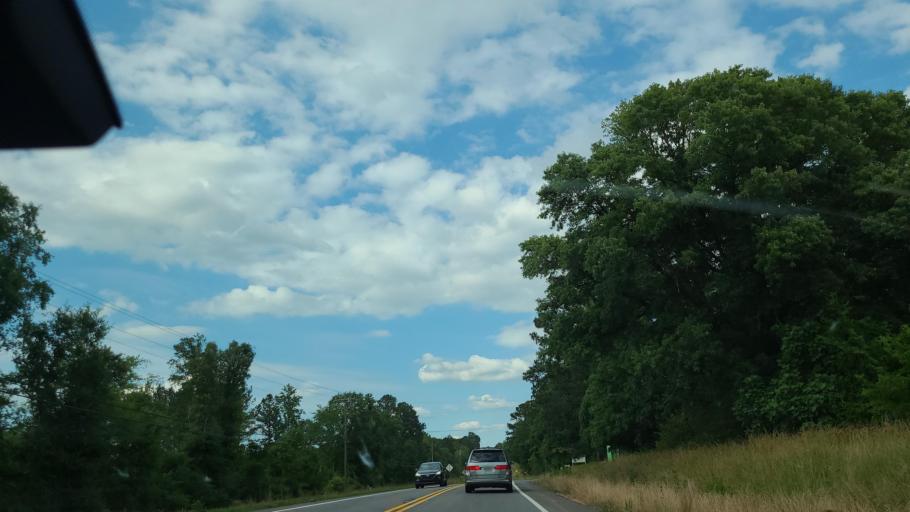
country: US
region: Georgia
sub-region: Putnam County
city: Eatonton
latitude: 33.2714
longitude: -83.4116
